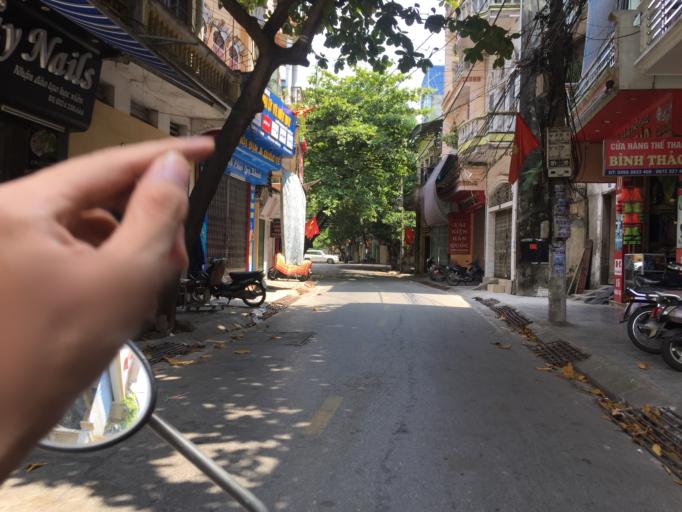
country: VN
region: Nam Dinh
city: Thanh Pho Nam Dinh
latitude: 20.4276
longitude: 106.1772
